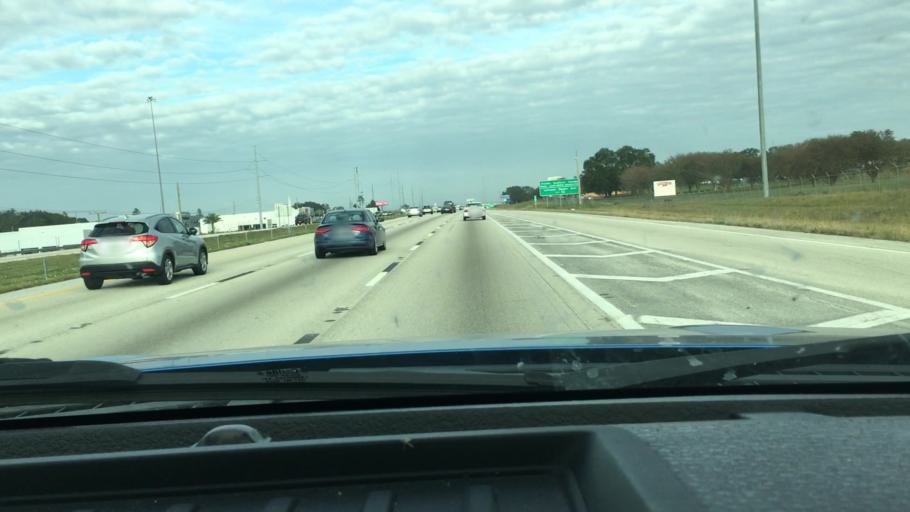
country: US
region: Florida
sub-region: Polk County
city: Gibsonia
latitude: 28.0745
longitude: -81.9843
